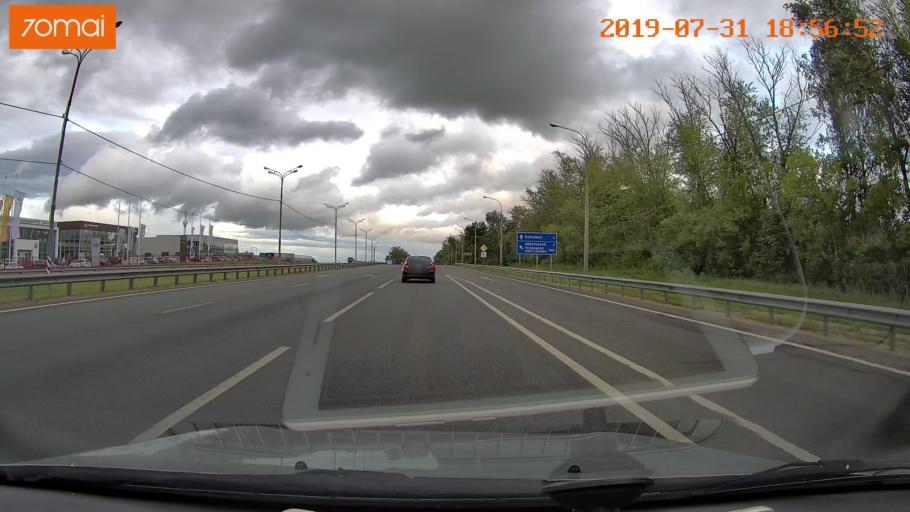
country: RU
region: Moskovskaya
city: Raduzhnyy
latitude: 55.1591
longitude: 38.6842
